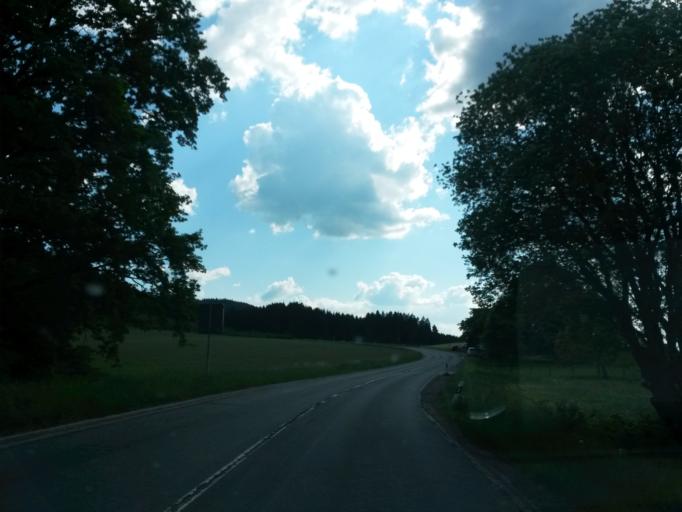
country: DE
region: North Rhine-Westphalia
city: Plettenberg
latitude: 51.2575
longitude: 7.8644
